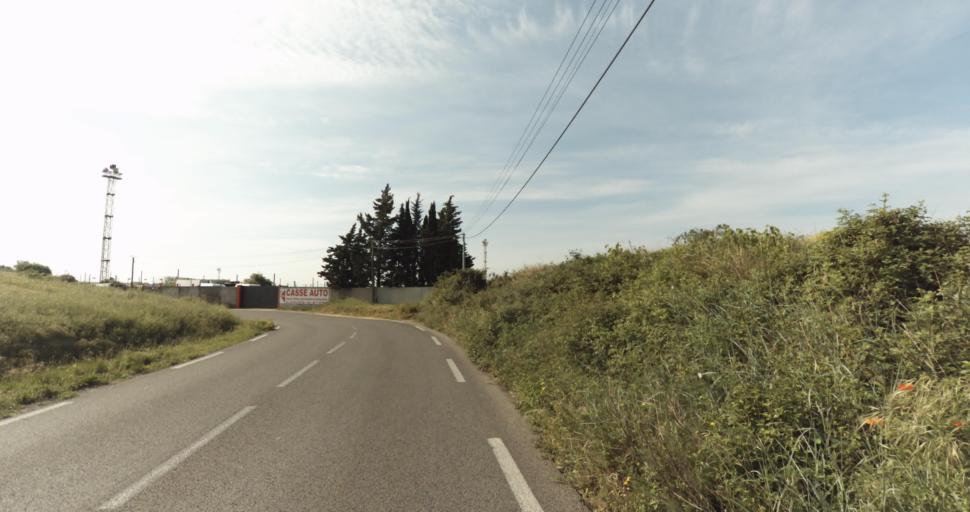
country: FR
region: Languedoc-Roussillon
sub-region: Departement du Gard
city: Rodilhan
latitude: 43.8485
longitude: 4.4094
